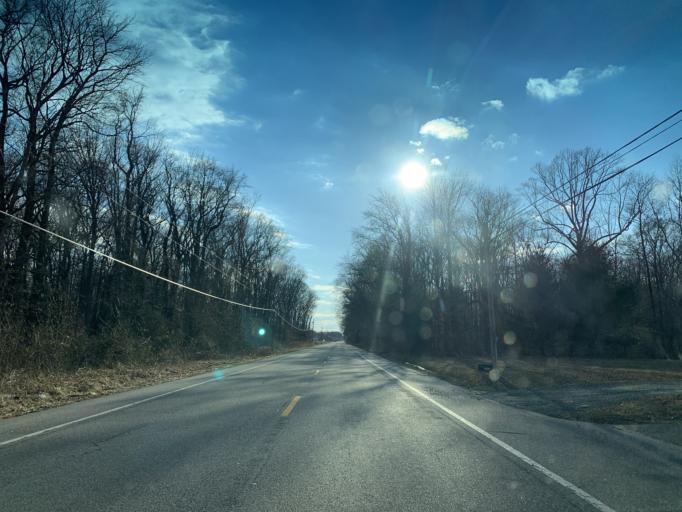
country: US
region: Maryland
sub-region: Queen Anne's County
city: Kingstown
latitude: 39.1680
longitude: -75.9288
